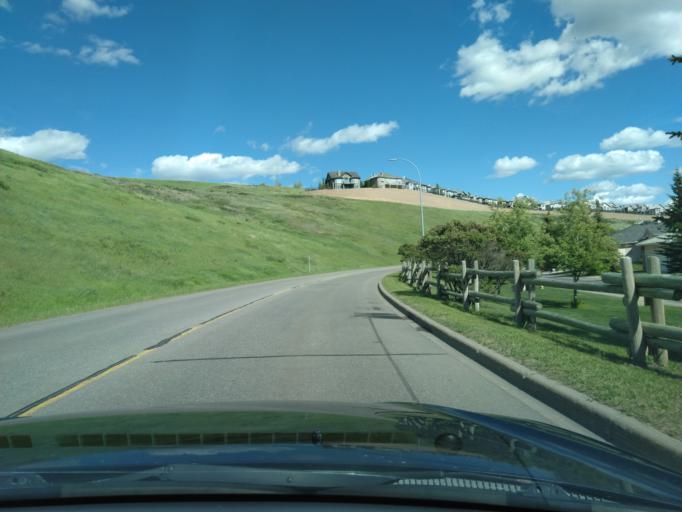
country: CA
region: Alberta
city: Cochrane
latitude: 51.1947
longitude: -114.4349
